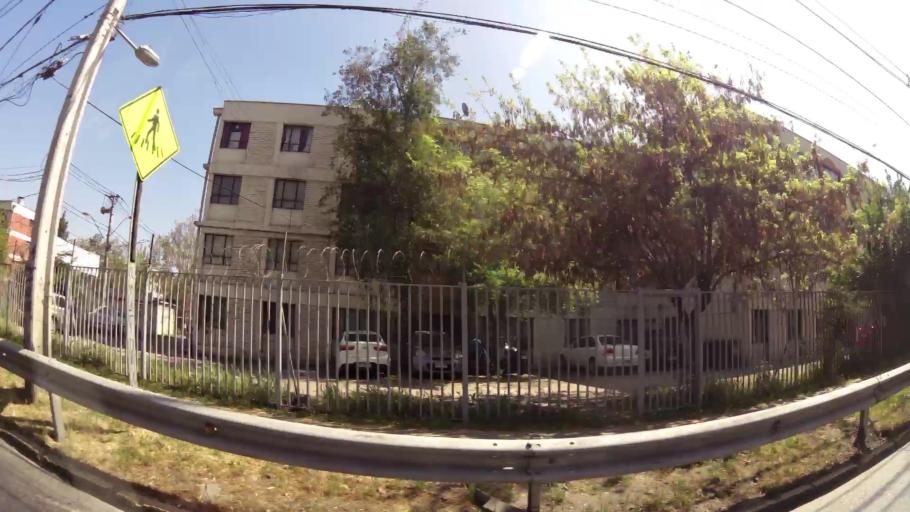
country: CL
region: Santiago Metropolitan
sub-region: Provincia de Santiago
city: Villa Presidente Frei, Nunoa, Santiago, Chile
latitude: -33.4672
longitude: -70.5505
